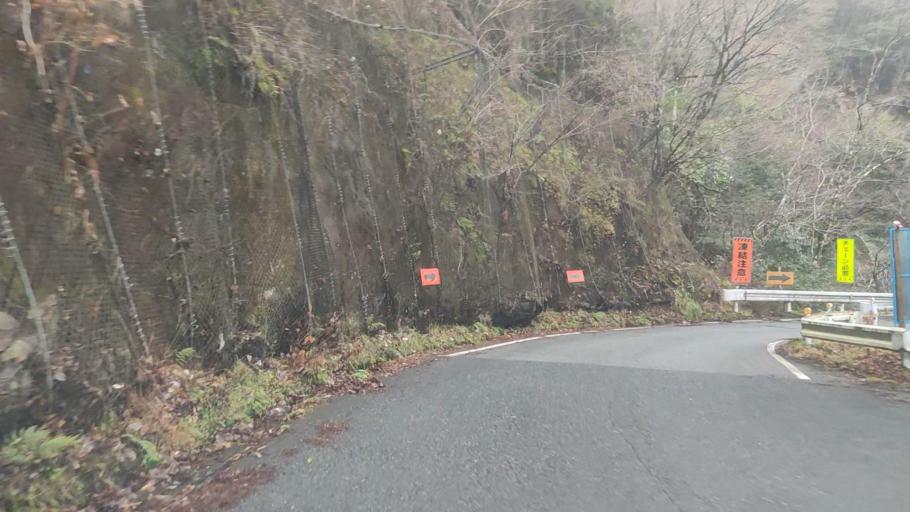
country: JP
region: Kumamoto
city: Matsubase
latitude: 32.4837
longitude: 130.8934
